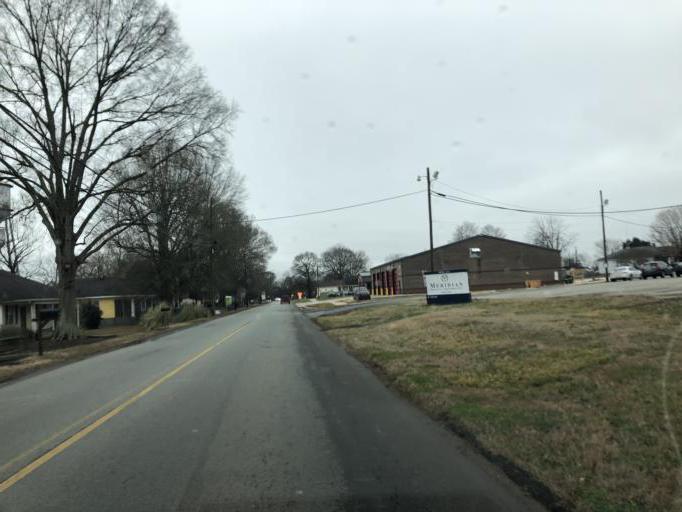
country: US
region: North Carolina
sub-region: Gaston County
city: Ranlo
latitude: 35.2893
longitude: -81.1280
